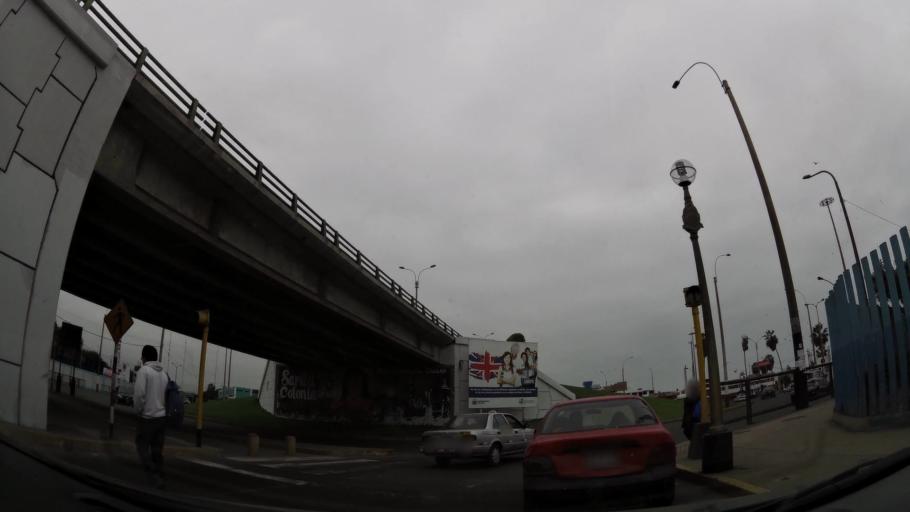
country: PE
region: Callao
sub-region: Callao
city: Callao
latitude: -12.0650
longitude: -77.1200
